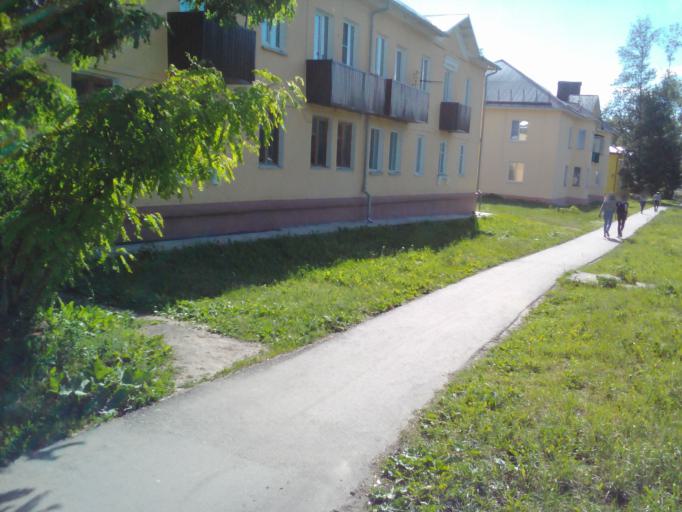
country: RU
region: Kursk
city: Voroshnevo
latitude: 51.6671
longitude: 36.1019
